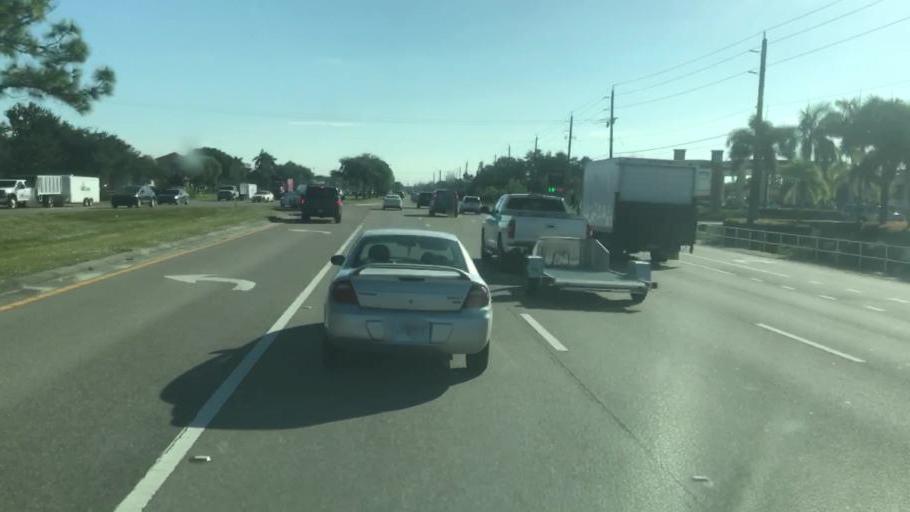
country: US
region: Florida
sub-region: Lee County
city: Villas
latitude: 26.5471
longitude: -81.8090
